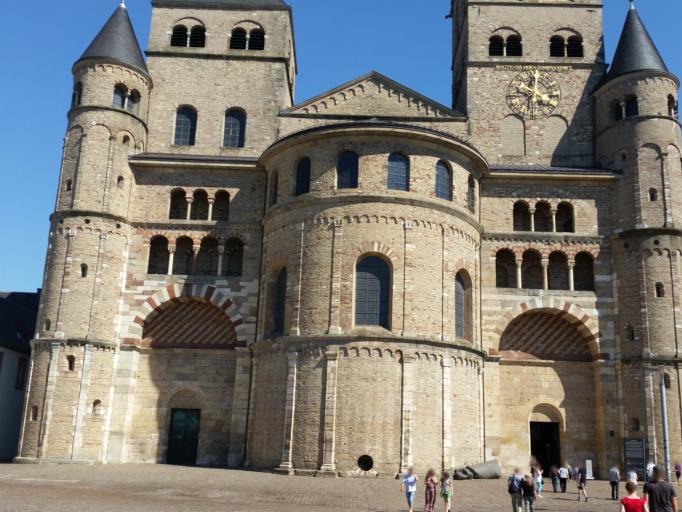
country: DE
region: Rheinland-Pfalz
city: Trier
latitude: 49.7565
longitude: 6.6423
